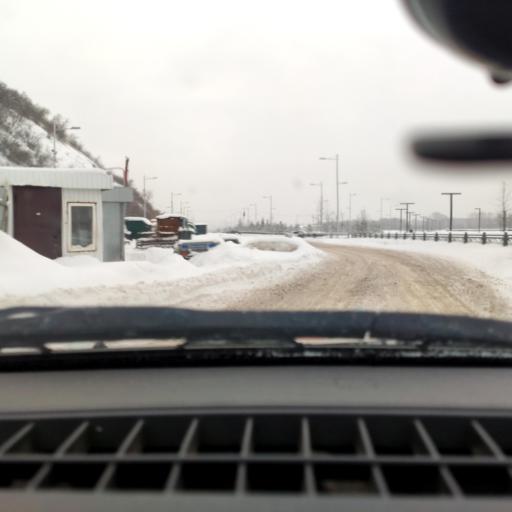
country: RU
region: Bashkortostan
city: Ufa
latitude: 54.7182
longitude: 55.9213
